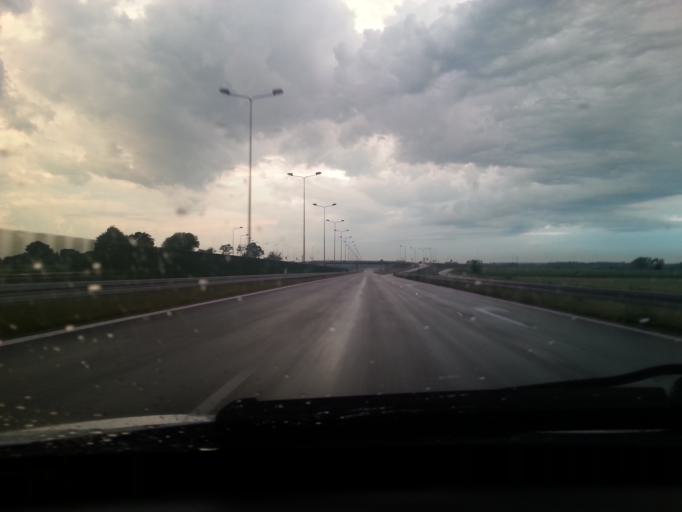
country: PL
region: Lodz Voivodeship
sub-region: Powiat pabianicki
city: Ksawerow
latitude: 51.6974
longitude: 19.3767
